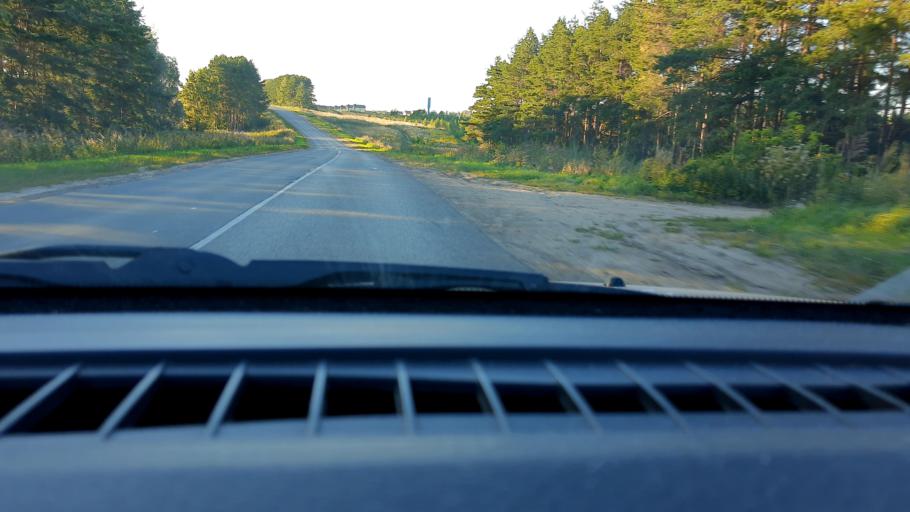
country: RU
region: Nizjnij Novgorod
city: Burevestnik
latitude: 56.1590
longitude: 43.7760
